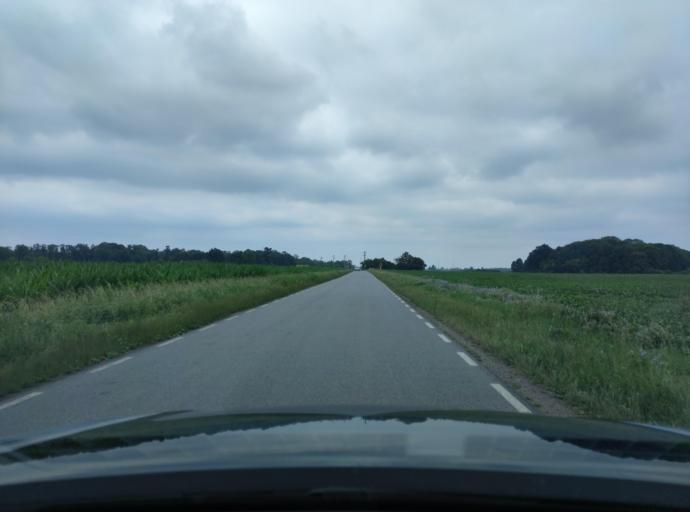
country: PL
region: Lower Silesian Voivodeship
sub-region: Powiat wroclawski
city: Kobierzyce
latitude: 50.9624
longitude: 16.8963
